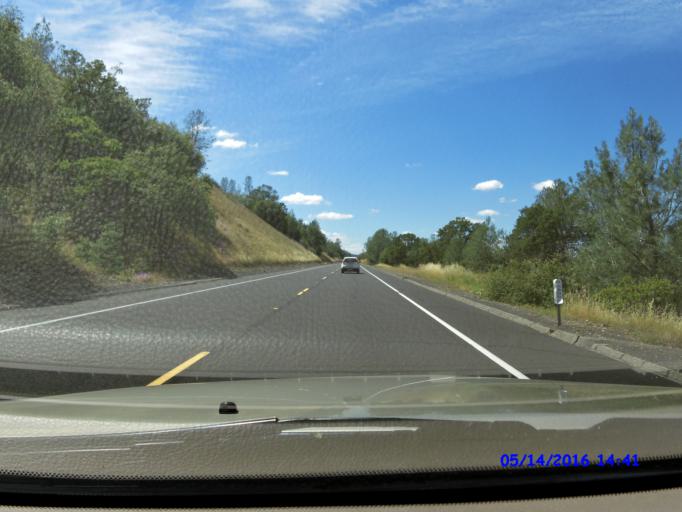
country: US
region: California
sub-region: Tuolumne County
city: East Sonora
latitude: 37.8241
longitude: -120.3341
